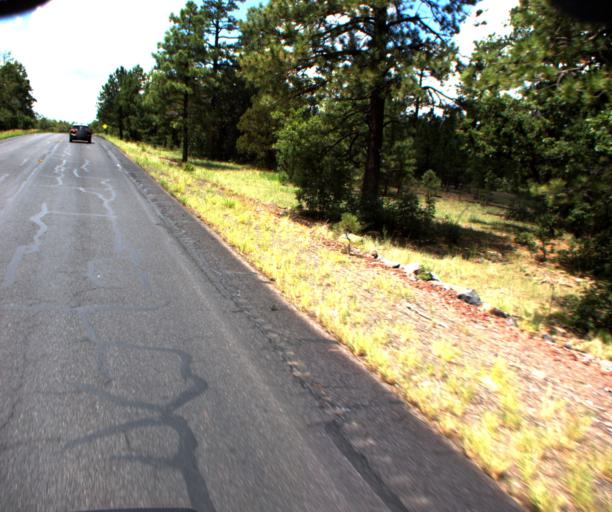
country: US
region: Arizona
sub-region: Gila County
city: Pine
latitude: 34.5046
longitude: -111.4693
